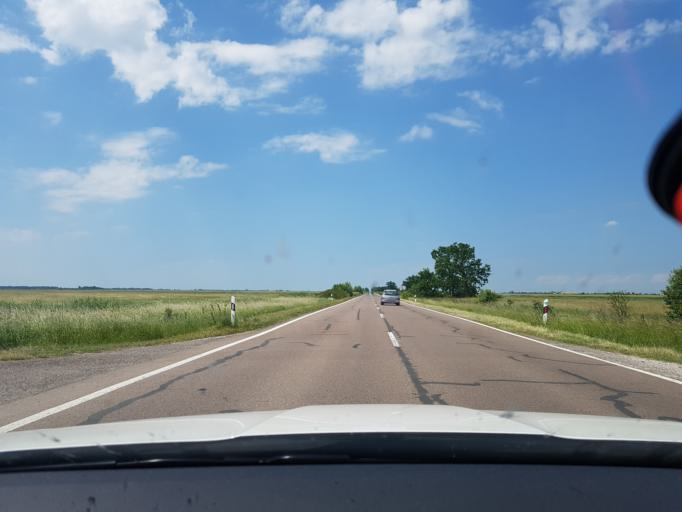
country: HU
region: Hajdu-Bihar
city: Hortobagy
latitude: 47.5826
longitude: 21.1341
